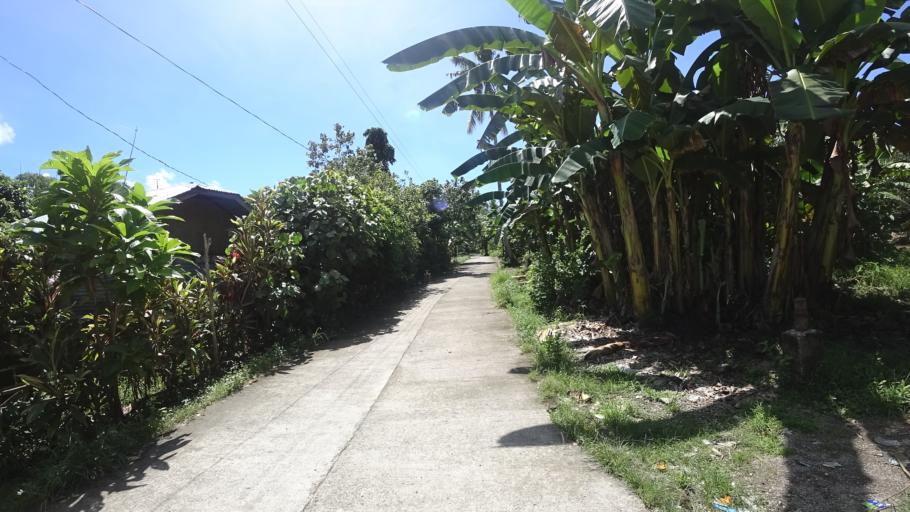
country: PH
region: Eastern Visayas
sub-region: Province of Leyte
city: Cabacungan
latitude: 10.9187
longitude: 124.9765
